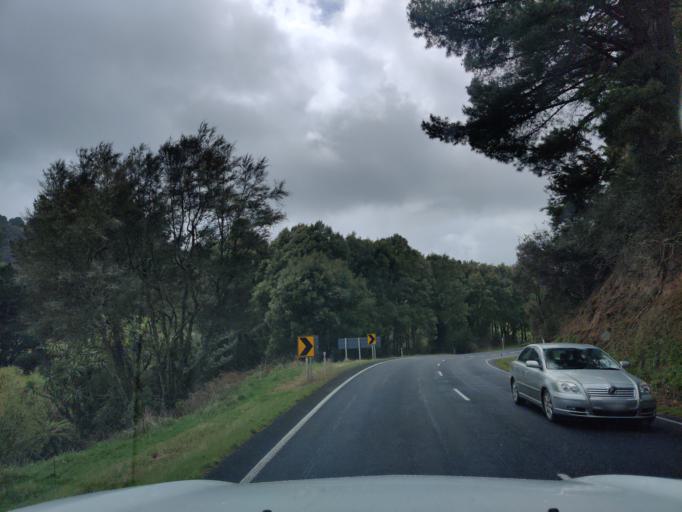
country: NZ
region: Waikato
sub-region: Otorohanga District
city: Otorohanga
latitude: -38.6969
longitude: 175.2238
